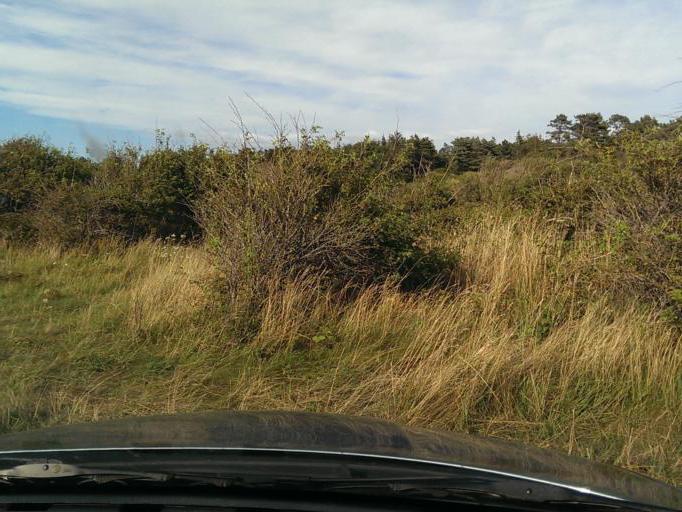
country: DK
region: Central Jutland
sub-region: Syddjurs Kommune
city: Ebeltoft
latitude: 56.0958
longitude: 10.5134
